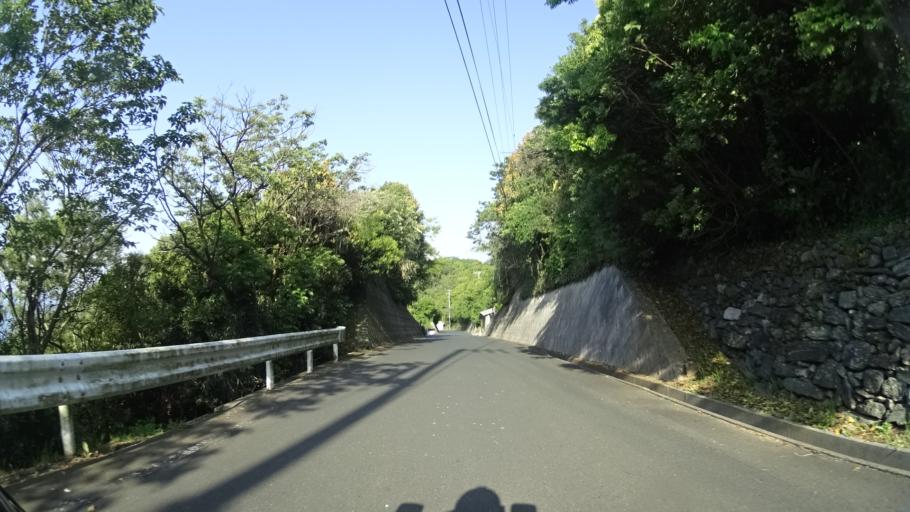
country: JP
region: Ehime
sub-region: Nishiuwa-gun
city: Ikata-cho
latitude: 33.3734
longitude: 132.0592
